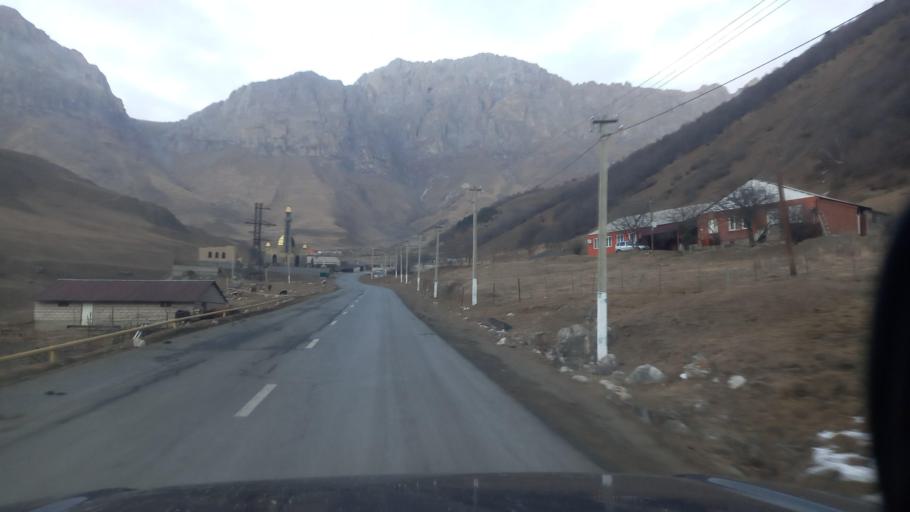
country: RU
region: Ingushetiya
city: Dzhayrakh
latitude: 42.8134
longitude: 44.8127
